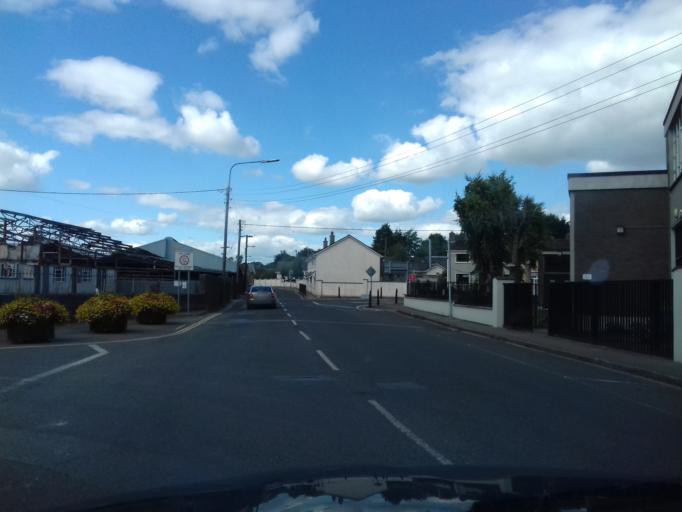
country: IE
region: Munster
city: Carrick-on-Suir
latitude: 52.3496
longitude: -7.4151
